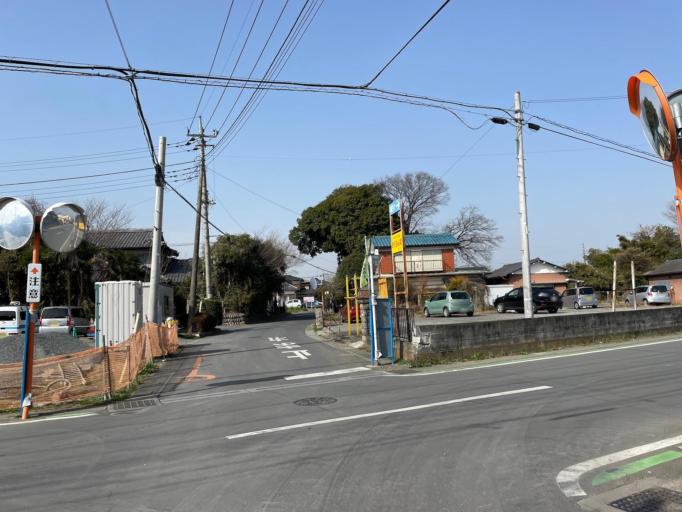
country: JP
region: Saitama
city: Yorii
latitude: 36.1079
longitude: 139.2326
